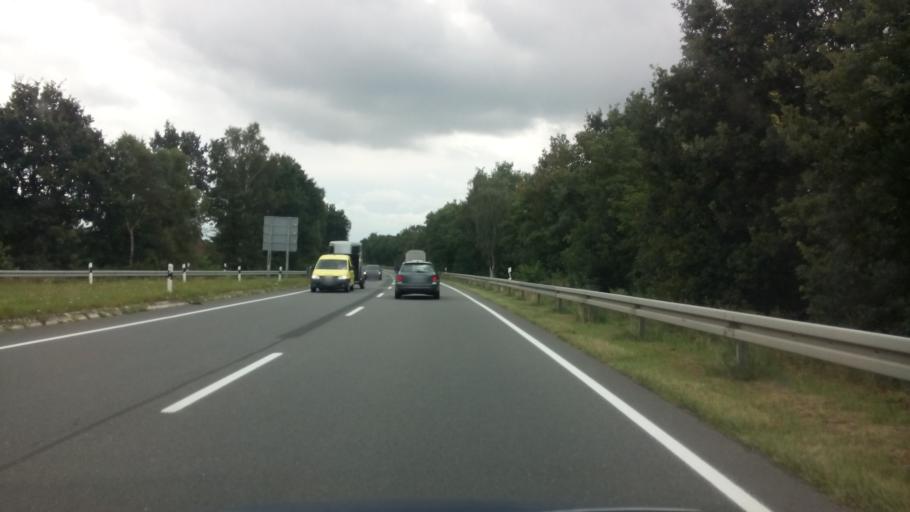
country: DE
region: Lower Saxony
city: Diepholz
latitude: 52.5927
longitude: 8.3556
